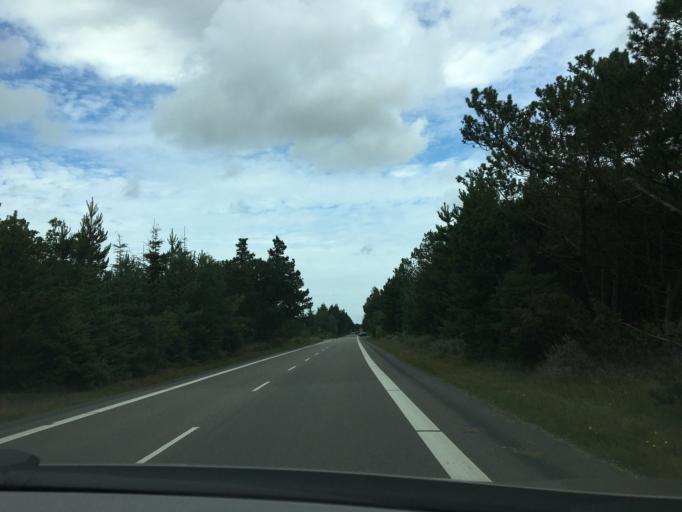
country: DK
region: South Denmark
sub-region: Varde Kommune
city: Oksbol
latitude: 55.7790
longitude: 8.2379
